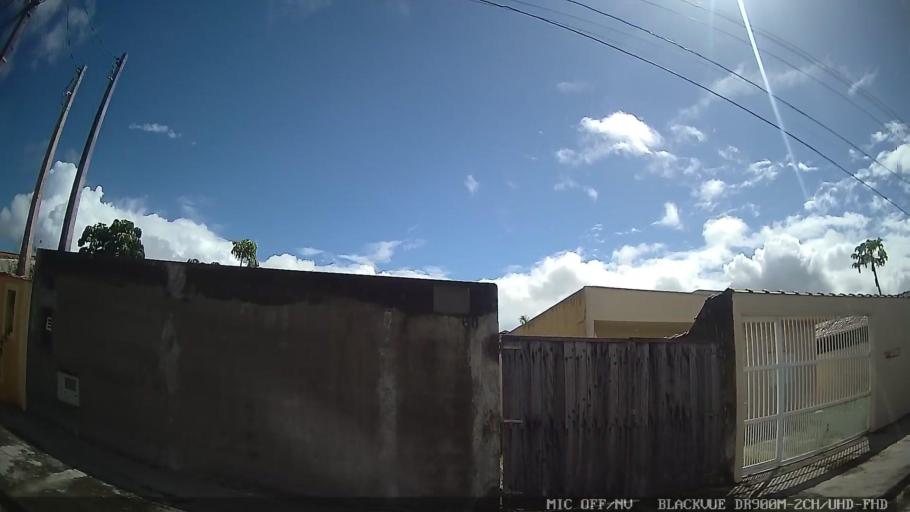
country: BR
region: Sao Paulo
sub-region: Itanhaem
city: Itanhaem
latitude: -24.2249
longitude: -46.8614
